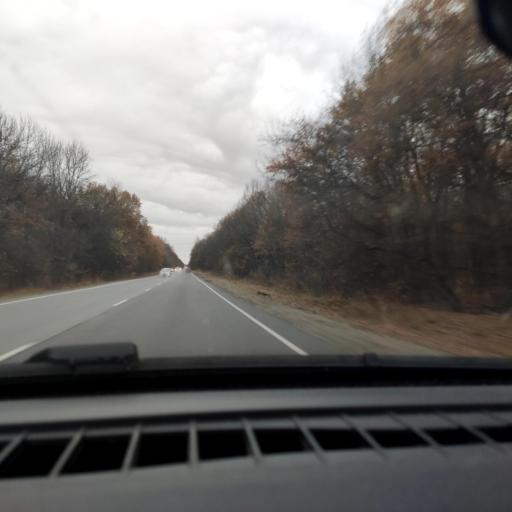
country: RU
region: Voronezj
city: Devitsa
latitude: 51.6271
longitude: 38.9898
